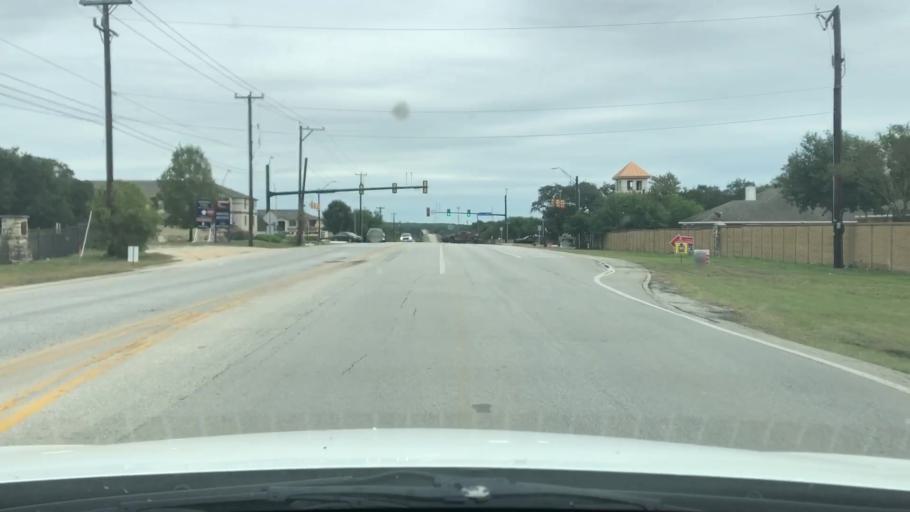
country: US
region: Texas
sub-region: Bexar County
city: Hollywood Park
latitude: 29.6455
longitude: -98.4035
